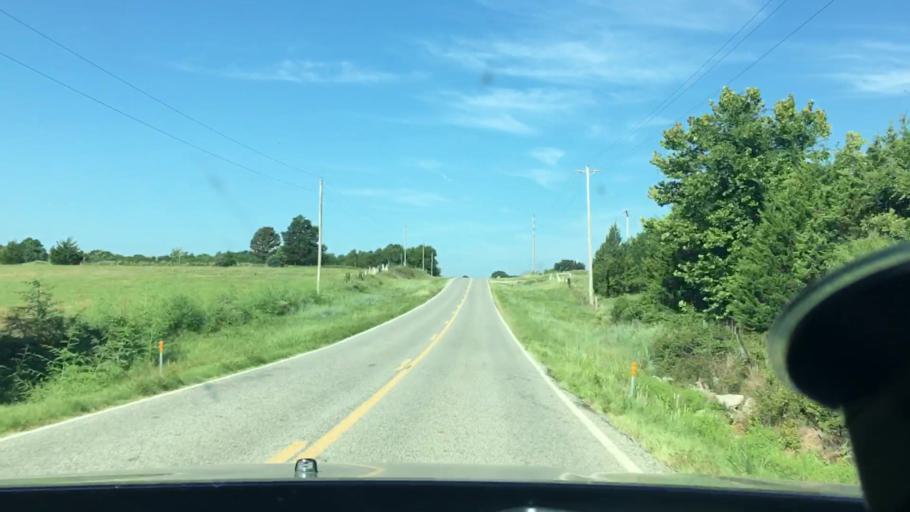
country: US
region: Oklahoma
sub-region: Johnston County
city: Tishomingo
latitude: 34.2742
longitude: -96.5207
